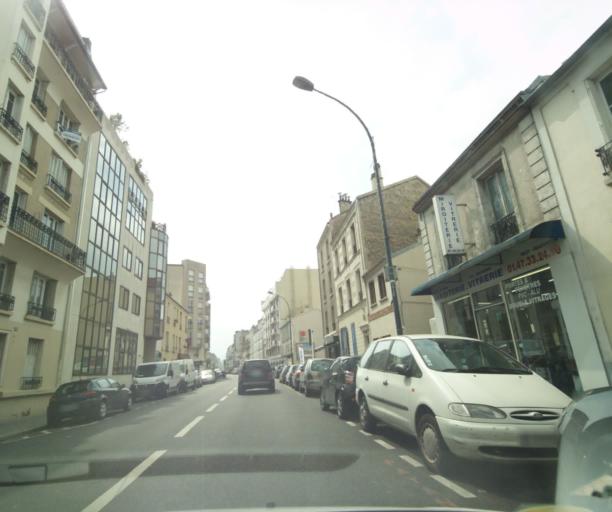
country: FR
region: Ile-de-France
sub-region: Departement des Hauts-de-Seine
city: Asnieres-sur-Seine
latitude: 48.9144
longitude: 2.2833
